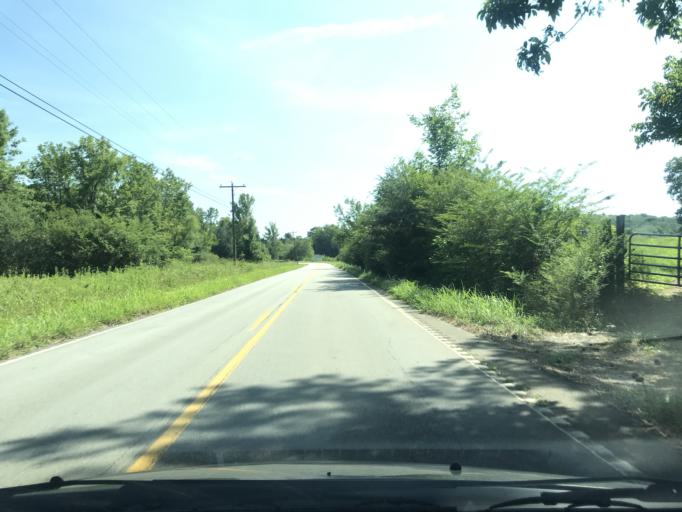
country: US
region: Tennessee
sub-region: Hamilton County
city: Sale Creek
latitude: 35.3324
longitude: -85.0094
